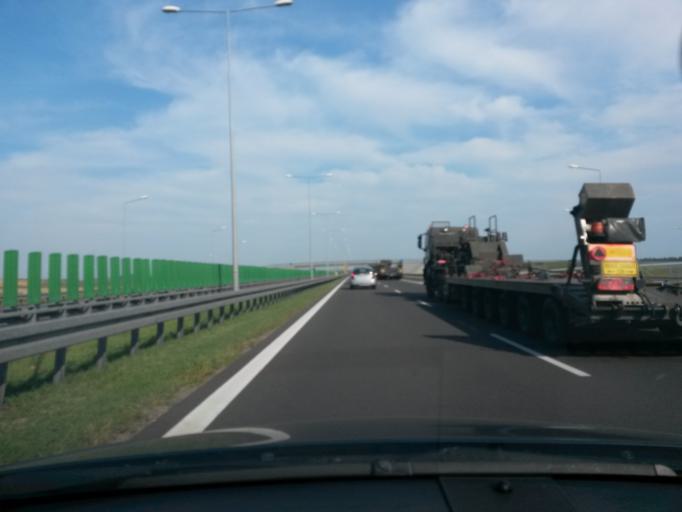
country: PL
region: Greater Poland Voivodeship
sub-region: Powiat slupecki
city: Strzalkowo
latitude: 52.2551
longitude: 17.8142
